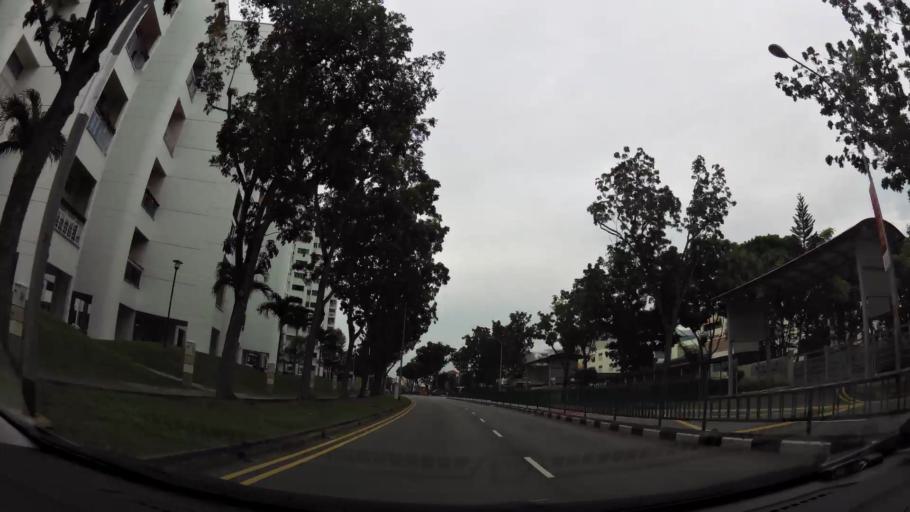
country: SG
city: Singapore
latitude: 1.3571
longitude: 103.8897
